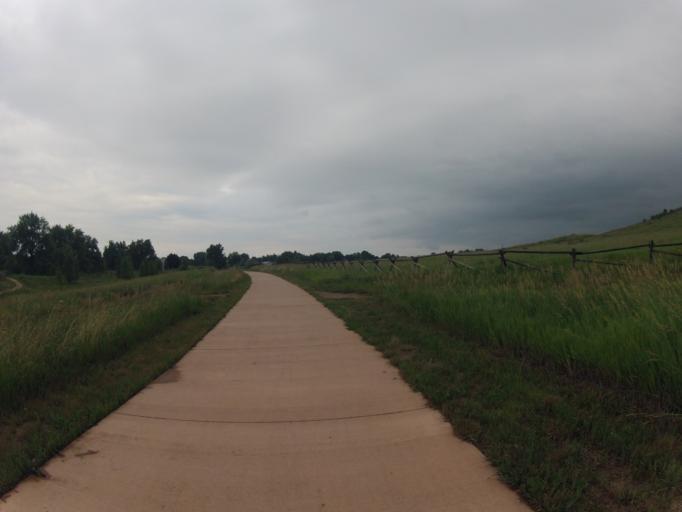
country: US
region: Colorado
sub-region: Larimer County
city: Fort Collins
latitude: 40.5383
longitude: -105.1285
